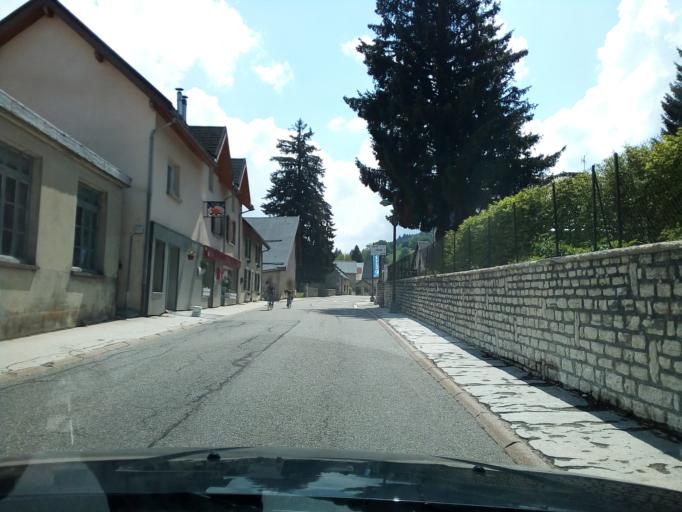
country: FR
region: Rhone-Alpes
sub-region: Departement de l'Isere
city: Meaudre
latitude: 45.1293
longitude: 5.5279
